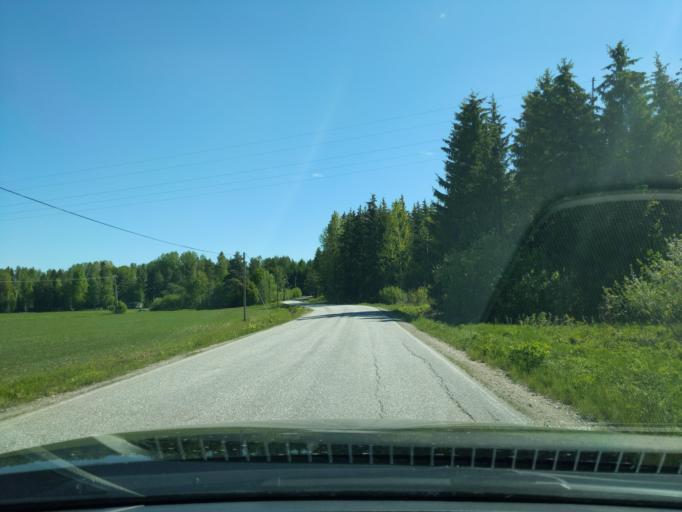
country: FI
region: Paijanne Tavastia
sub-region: Lahti
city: Lahti
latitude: 61.0614
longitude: 25.6786
